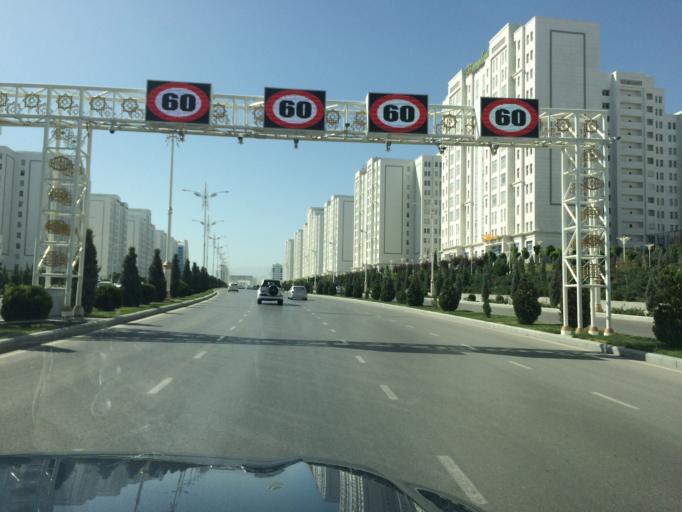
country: TM
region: Ahal
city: Ashgabat
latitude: 37.9377
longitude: 58.3648
